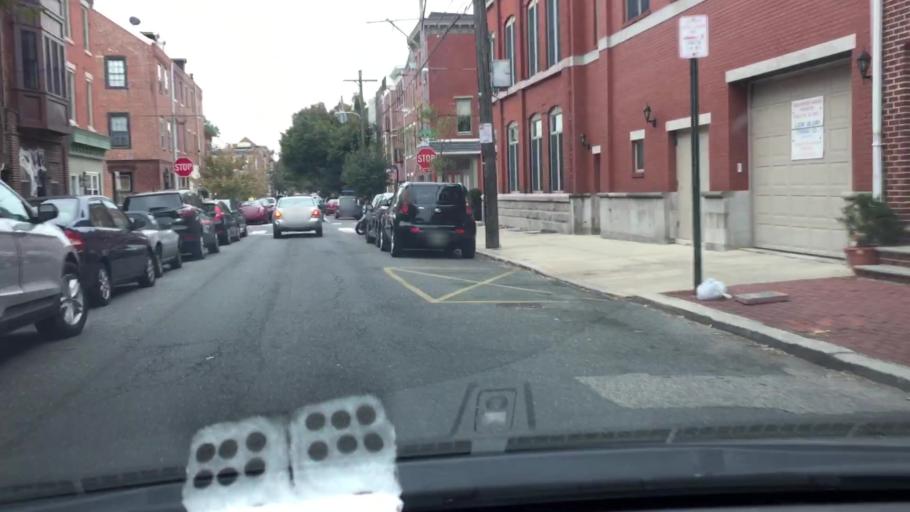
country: US
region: Pennsylvania
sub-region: Philadelphia County
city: Philadelphia
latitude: 39.9374
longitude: -75.1466
